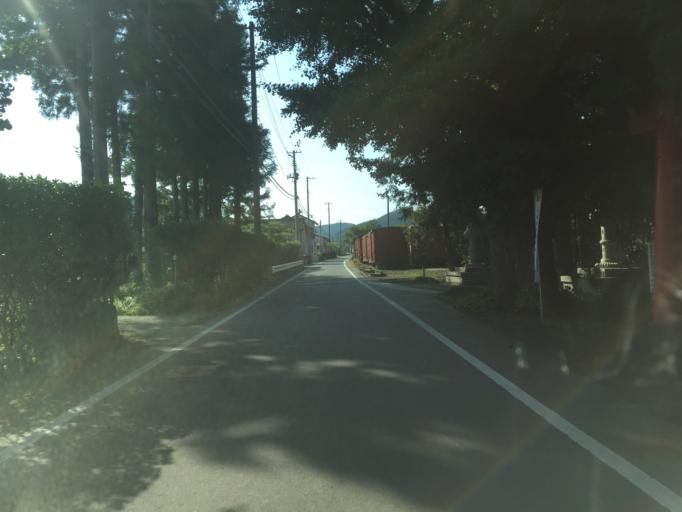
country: JP
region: Miyagi
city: Marumori
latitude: 37.8174
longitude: 140.8931
